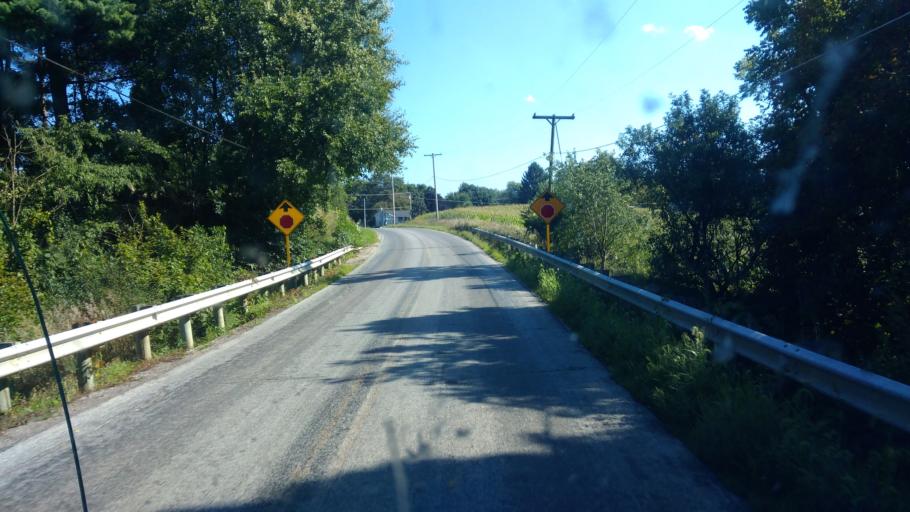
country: US
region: Ohio
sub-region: Ashland County
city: Ashland
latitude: 40.8897
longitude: -82.4273
